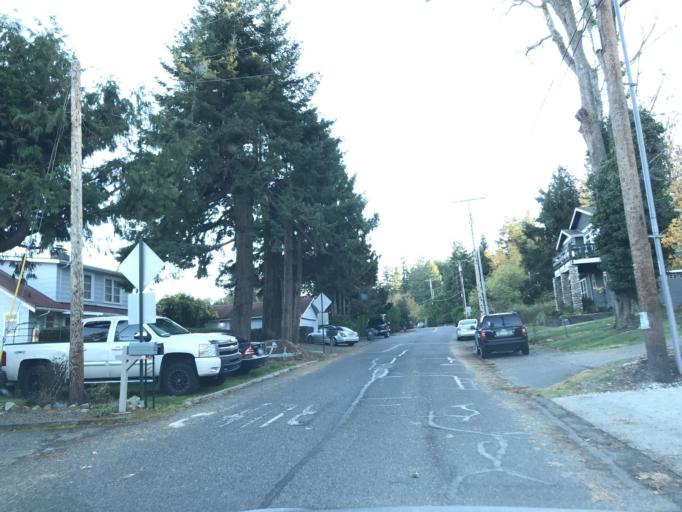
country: US
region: Washington
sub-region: Whatcom County
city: Geneva
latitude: 48.7540
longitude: -122.4123
